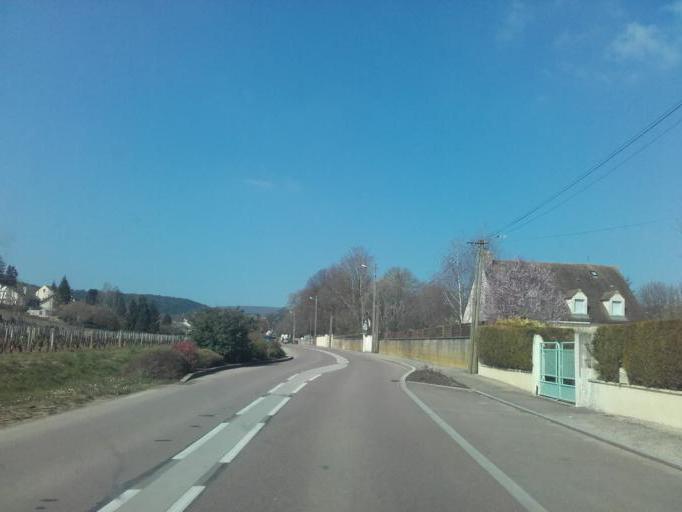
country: FR
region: Bourgogne
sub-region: Departement de la Cote-d'Or
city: Savigny-les-Beaune
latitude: 47.0590
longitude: 4.8282
